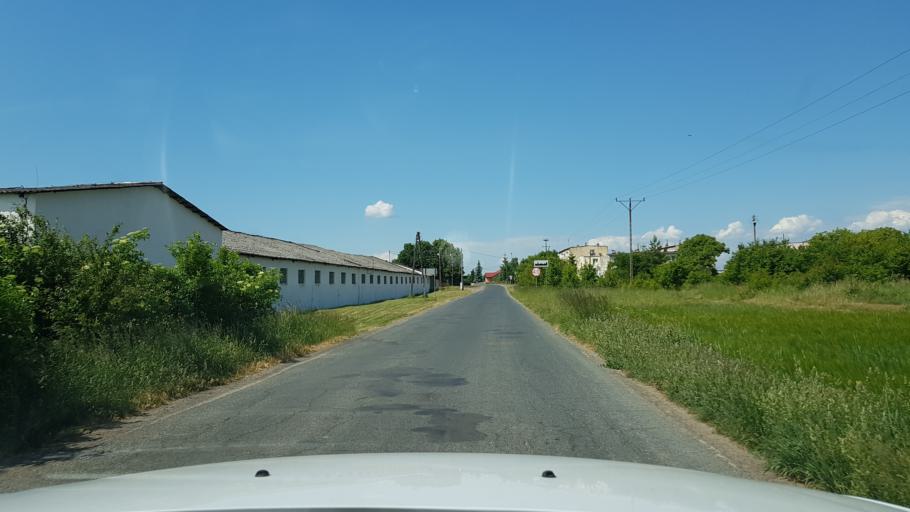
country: PL
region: West Pomeranian Voivodeship
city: Trzcinsko Zdroj
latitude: 53.0156
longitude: 14.5627
